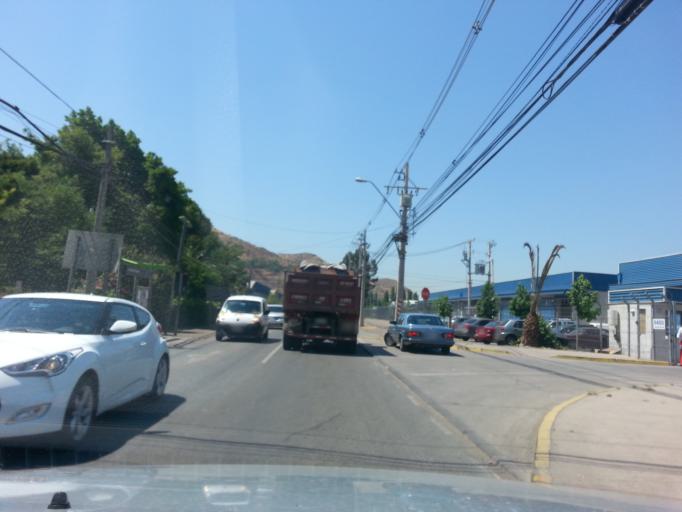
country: CL
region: Santiago Metropolitan
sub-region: Provincia de Chacabuco
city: Chicureo Abajo
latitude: -33.3353
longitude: -70.6968
